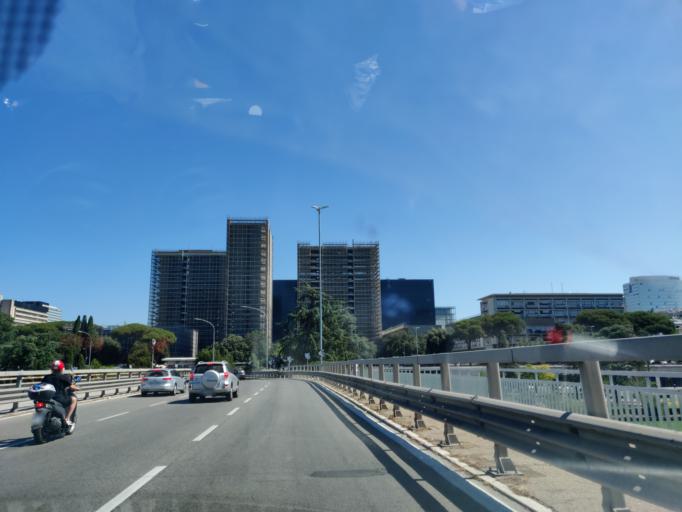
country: IT
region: Latium
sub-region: Citta metropolitana di Roma Capitale
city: Selcetta
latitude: 41.8275
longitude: 12.4696
